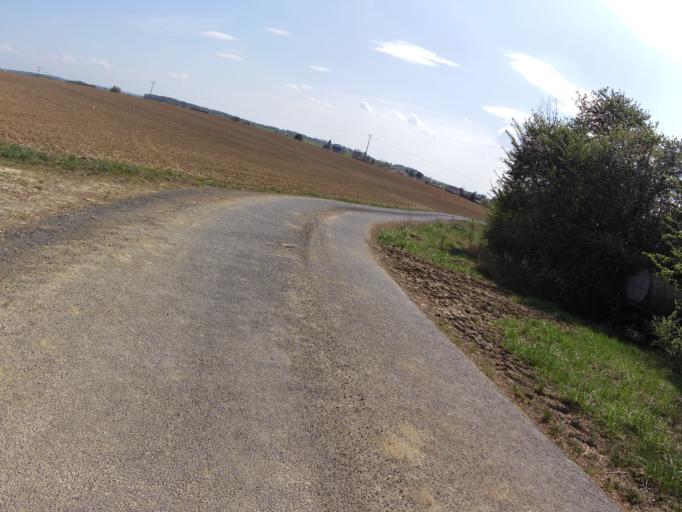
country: DE
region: Bavaria
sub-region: Regierungsbezirk Unterfranken
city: Giebelstadt
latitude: 49.6775
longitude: 9.9561
